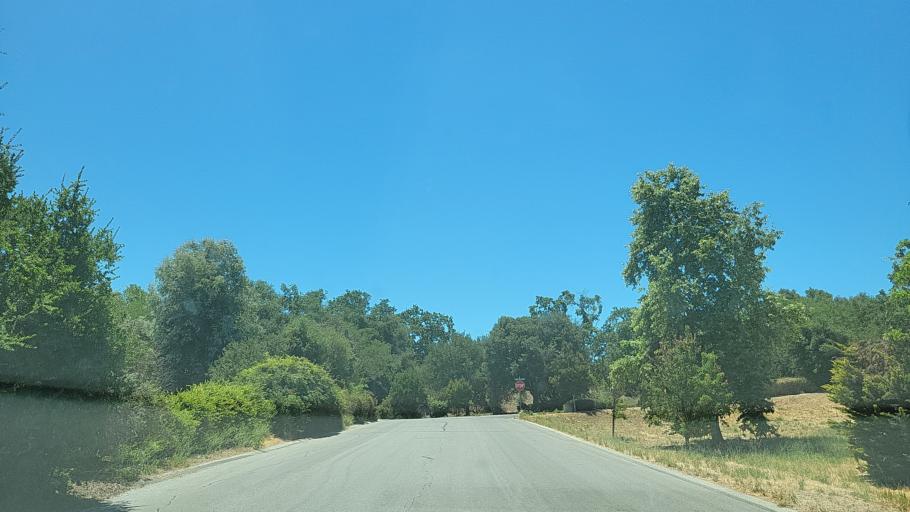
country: US
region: California
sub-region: San Luis Obispo County
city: Atascadero
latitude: 35.5152
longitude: -120.6773
